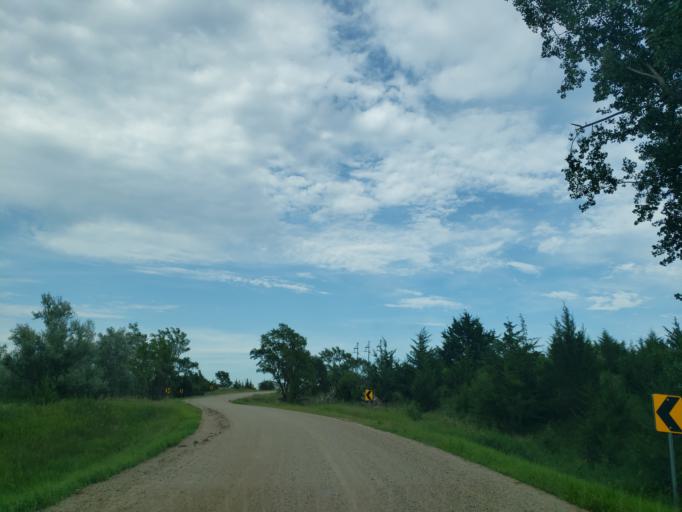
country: US
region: South Dakota
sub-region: Davison County
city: Mitchell
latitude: 43.6874
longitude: -97.9787
